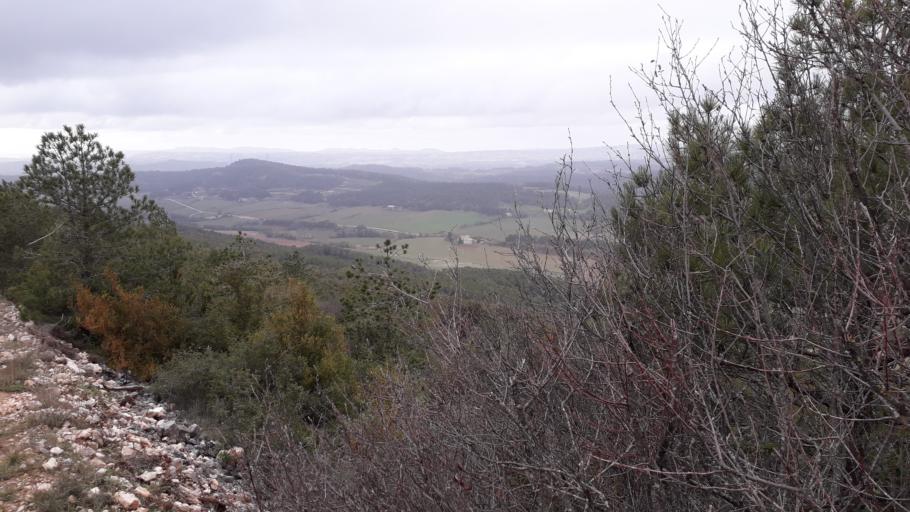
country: ES
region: Catalonia
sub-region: Provincia de Barcelona
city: Bellprat
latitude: 41.4890
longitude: 1.4628
